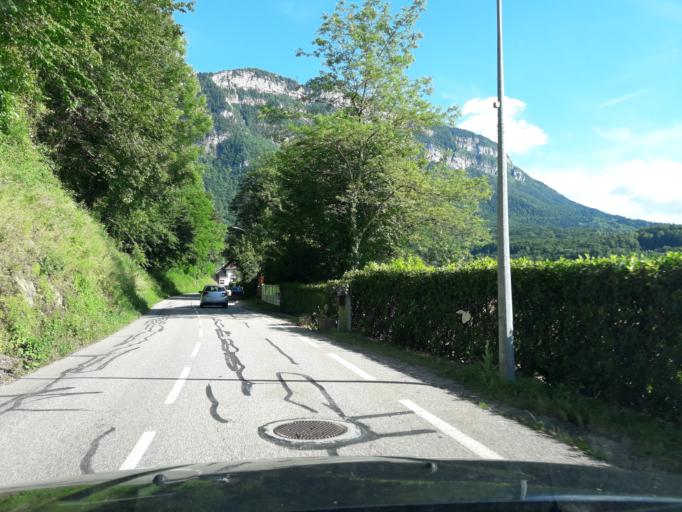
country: FR
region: Rhone-Alpes
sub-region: Departement de la Savoie
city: Vimines
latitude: 45.5466
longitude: 5.8112
